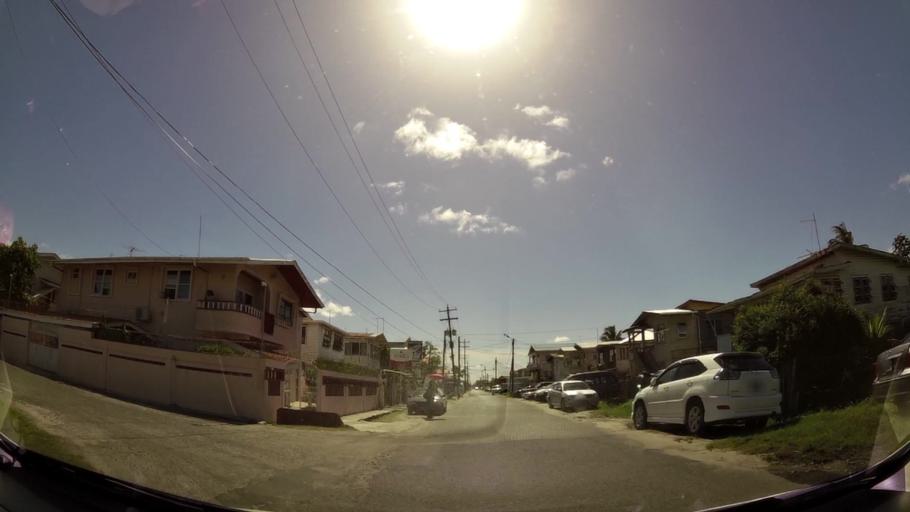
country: GY
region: Demerara-Mahaica
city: Georgetown
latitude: 6.8084
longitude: -58.1343
